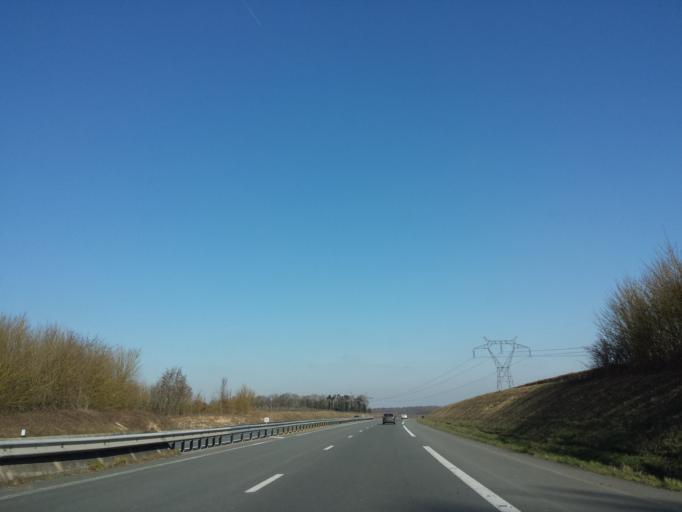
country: FR
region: Picardie
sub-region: Departement de la Somme
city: Saleux
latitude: 49.8173
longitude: 2.2452
